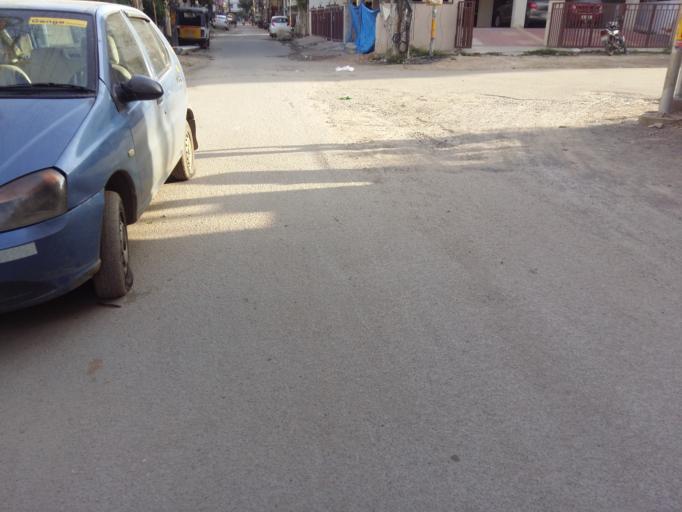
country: IN
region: Telangana
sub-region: Rangareddi
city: Kukatpalli
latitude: 17.4881
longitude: 78.3985
